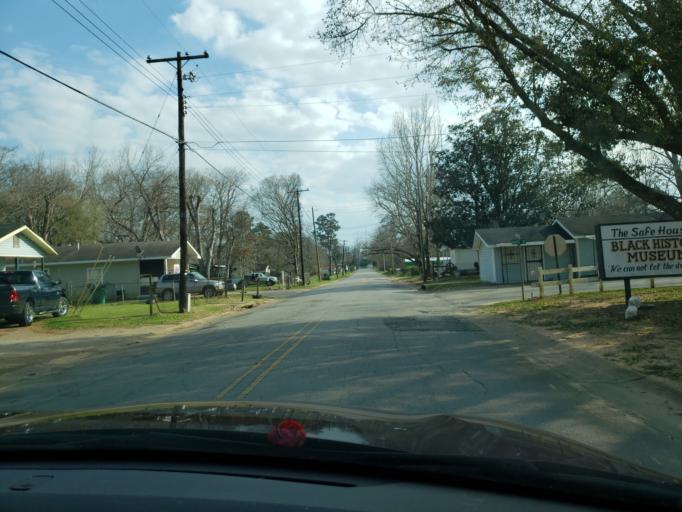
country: US
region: Alabama
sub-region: Hale County
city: Greensboro
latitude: 32.6978
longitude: -87.6094
